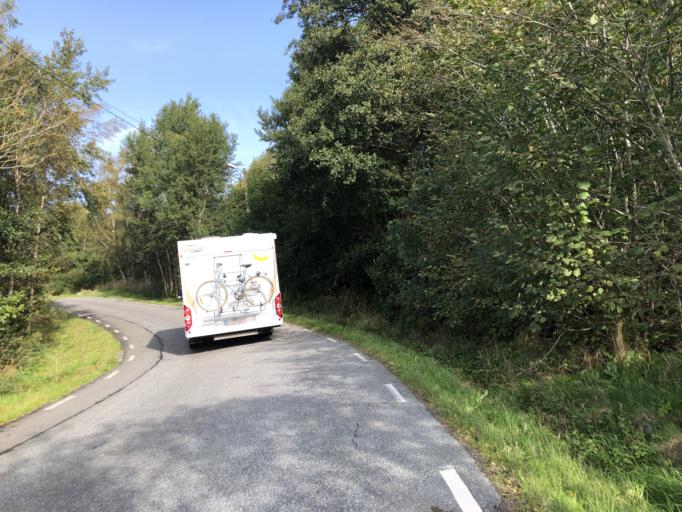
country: SE
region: Vaestra Goetaland
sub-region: Goteborg
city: Torslanda
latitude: 57.7333
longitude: 11.8444
